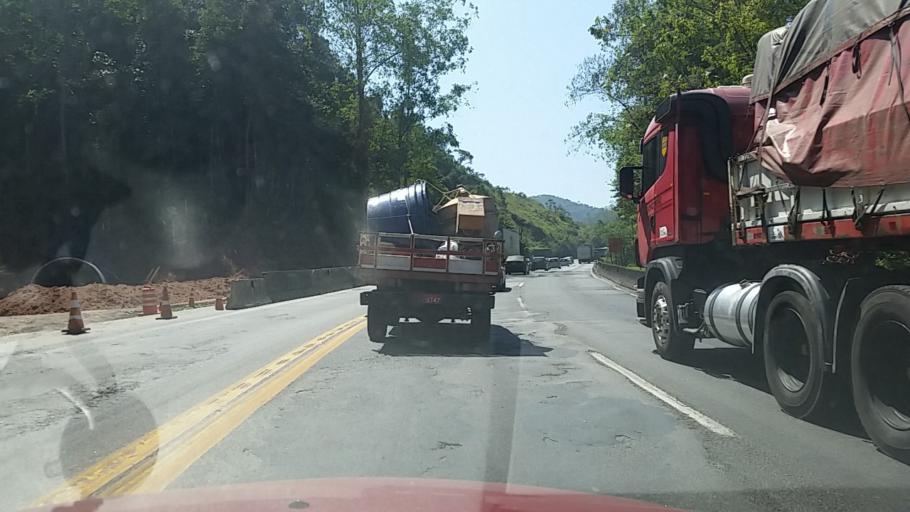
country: BR
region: Sao Paulo
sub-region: Juquitiba
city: Juquitiba
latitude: -24.1013
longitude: -47.2565
